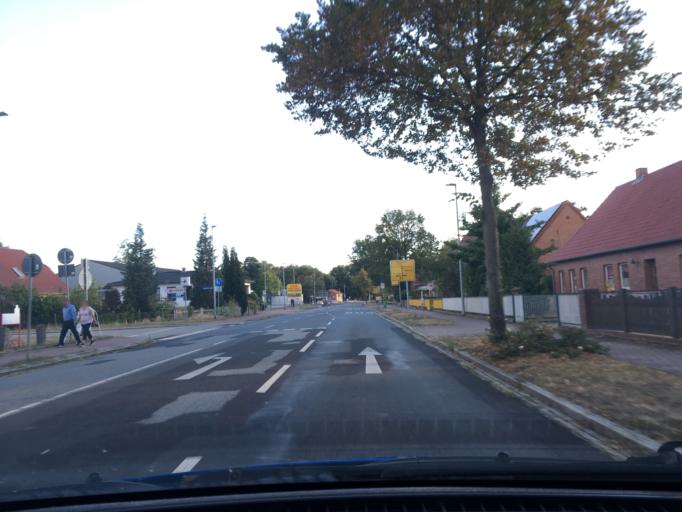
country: DE
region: Mecklenburg-Vorpommern
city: Neu Kaliss
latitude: 53.1795
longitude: 11.2921
